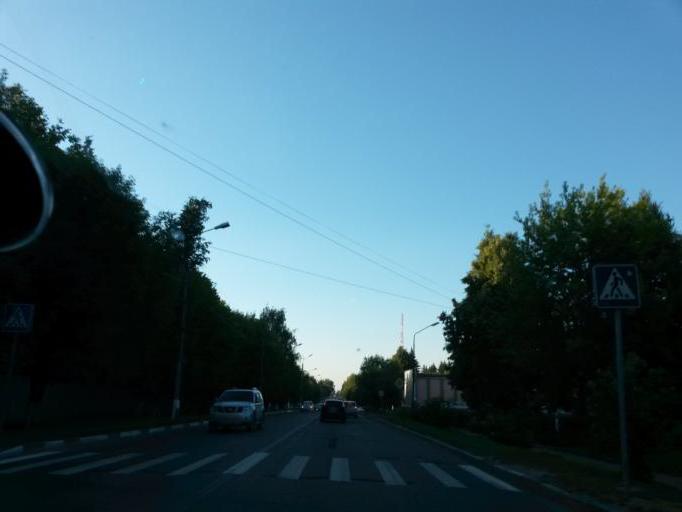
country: RU
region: Moskovskaya
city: Serpukhov
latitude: 54.9300
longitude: 37.4041
